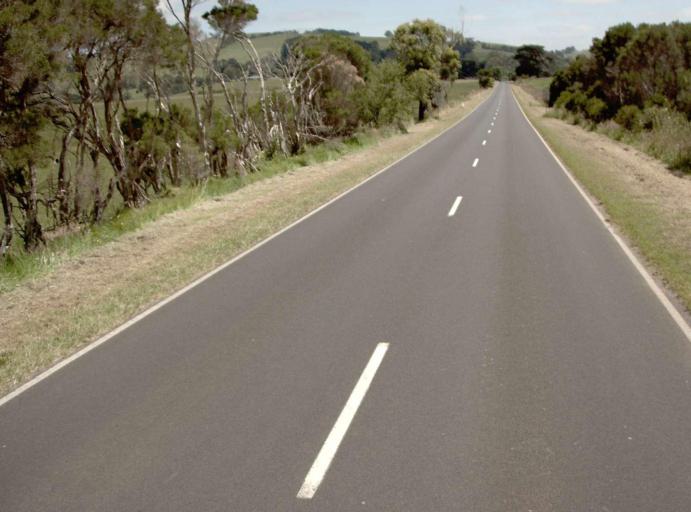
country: AU
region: Victoria
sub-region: Latrobe
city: Moe
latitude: -38.5307
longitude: 146.0894
